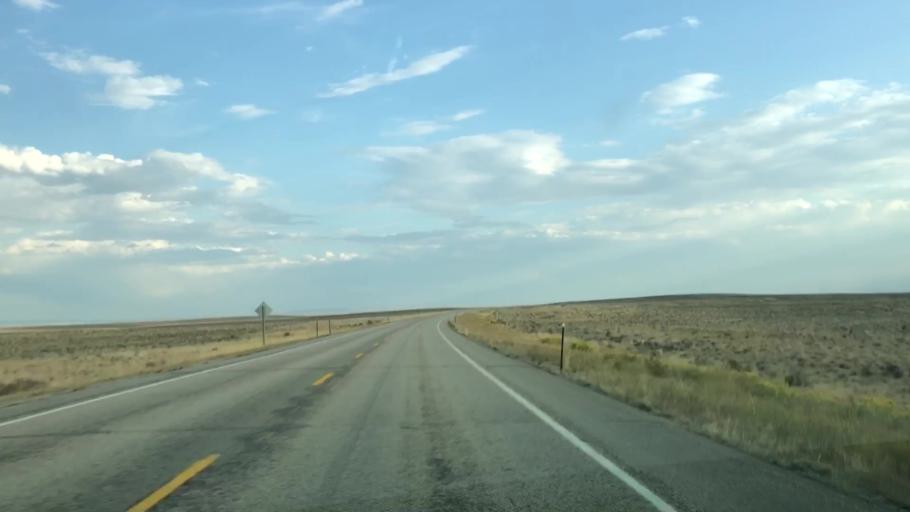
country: US
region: Wyoming
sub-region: Sweetwater County
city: North Rock Springs
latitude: 42.2558
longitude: -109.4689
